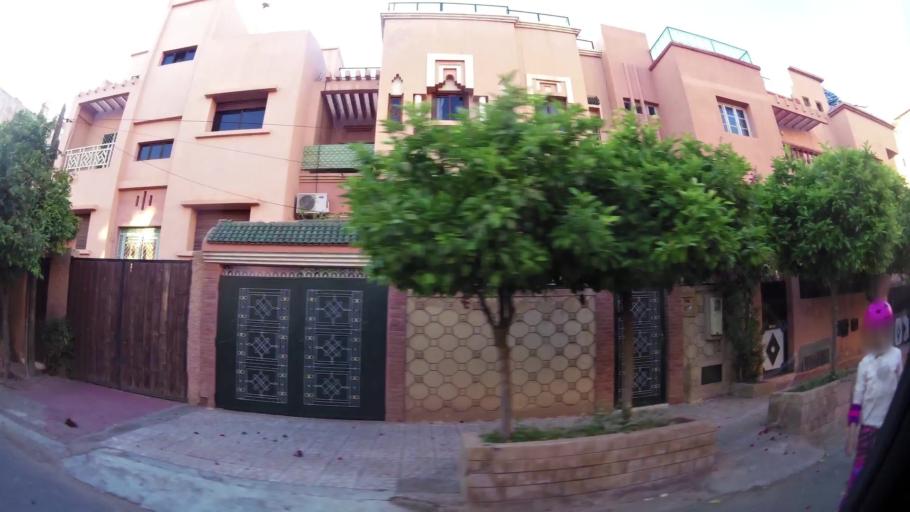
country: MA
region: Marrakech-Tensift-Al Haouz
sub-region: Marrakech
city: Marrakesh
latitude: 31.6219
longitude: -8.0291
